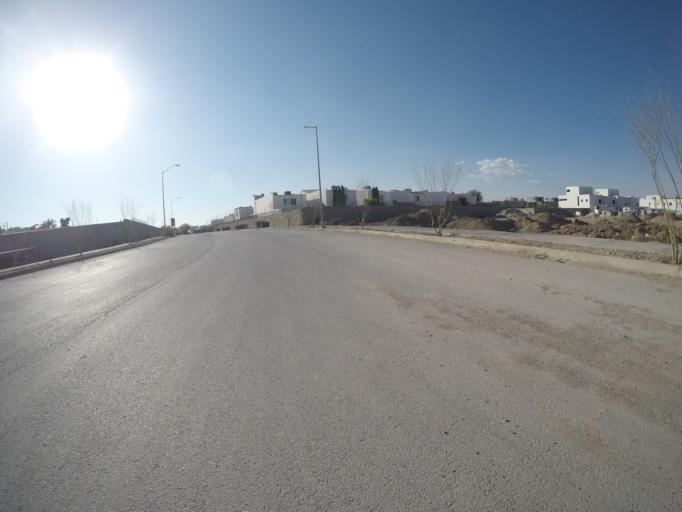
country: MX
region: Chihuahua
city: Ciudad Juarez
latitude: 31.7029
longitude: -106.3925
